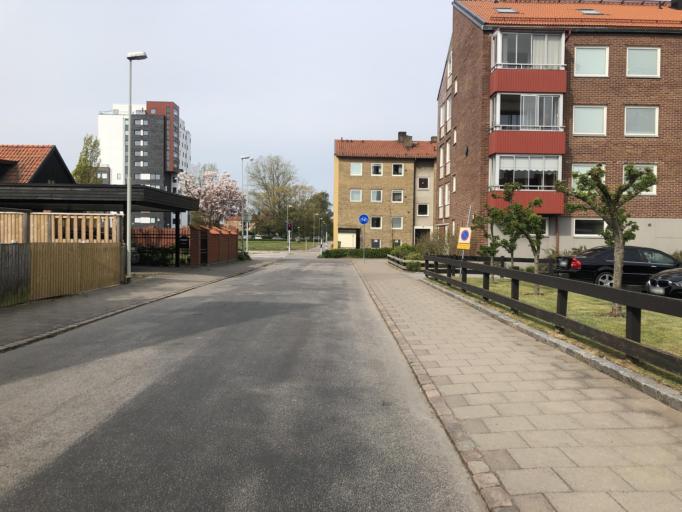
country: SE
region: Skane
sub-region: Landskrona
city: Landskrona
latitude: 55.8801
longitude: 12.8342
